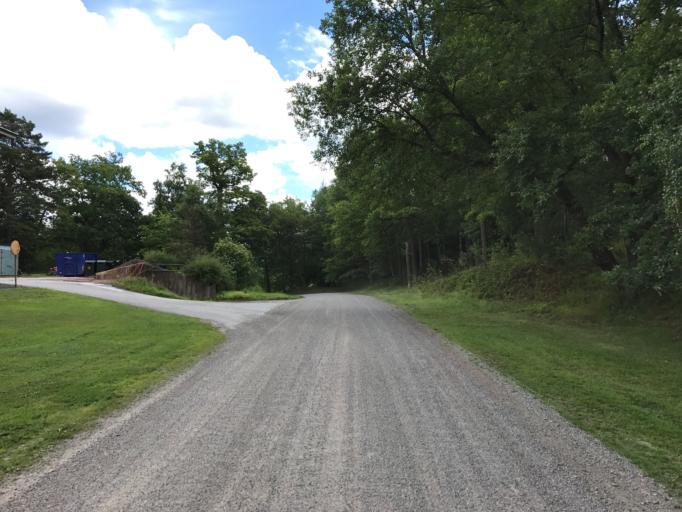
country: SE
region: Stockholm
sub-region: Lidingo
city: Lidingoe
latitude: 59.3274
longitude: 18.1250
